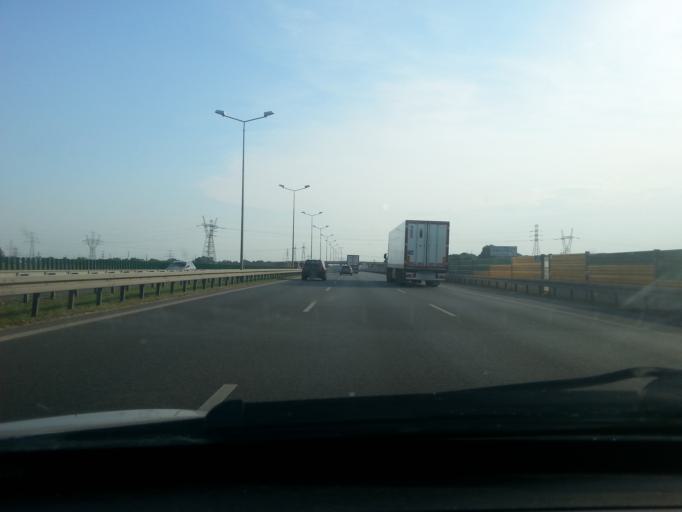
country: PL
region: Masovian Voivodeship
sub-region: Warszawa
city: Ursus
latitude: 52.2267
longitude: 20.8749
